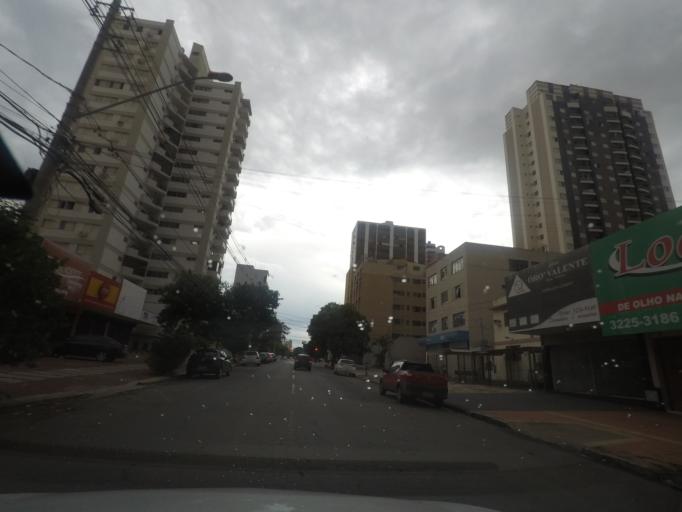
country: BR
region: Goias
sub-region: Goiania
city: Goiania
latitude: -16.6797
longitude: -49.2702
